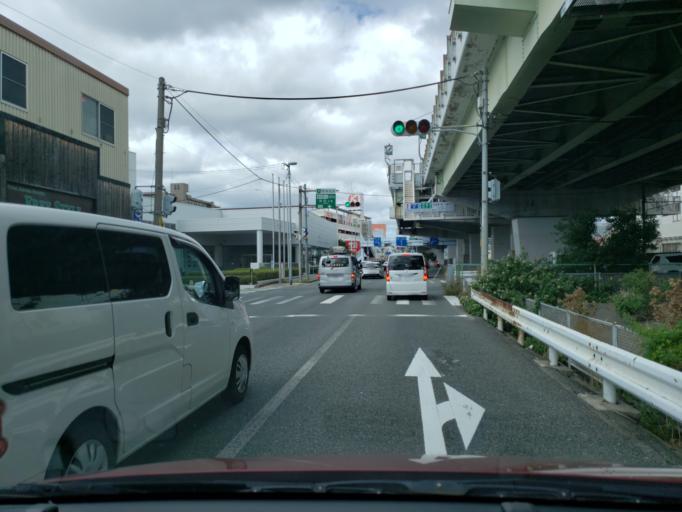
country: JP
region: Osaka
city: Toyonaka
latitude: 34.7566
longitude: 135.4621
